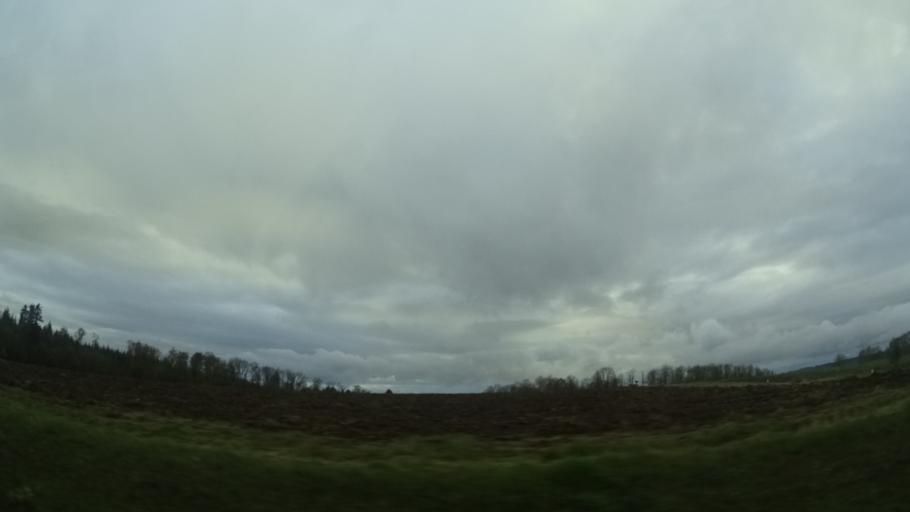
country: DE
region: Hesse
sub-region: Regierungsbezirk Giessen
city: Freiensteinau
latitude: 50.4569
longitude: 9.3929
